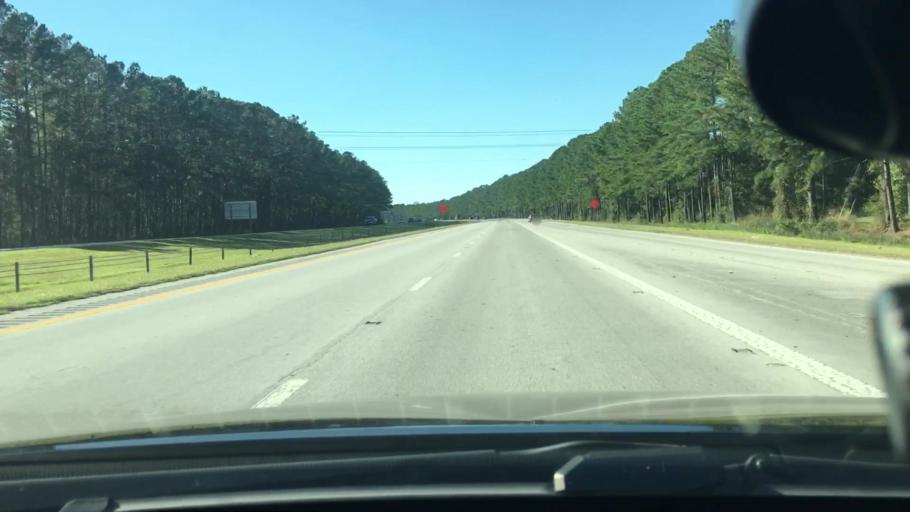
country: US
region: North Carolina
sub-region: Craven County
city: Trent Woods
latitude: 35.1146
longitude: -77.1001
